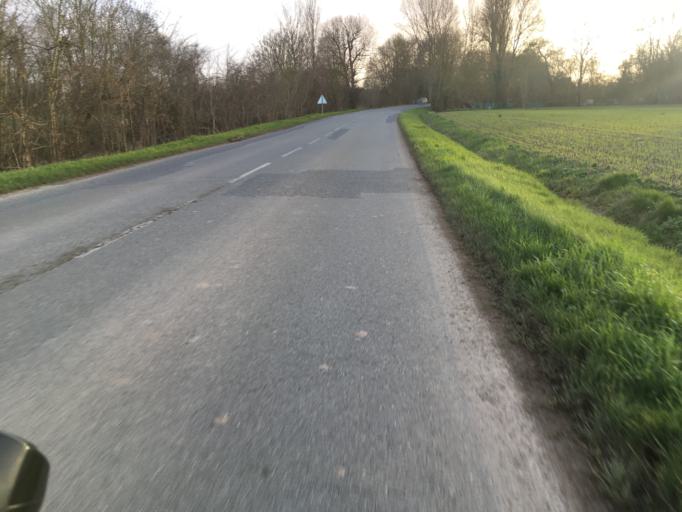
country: FR
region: Poitou-Charentes
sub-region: Departement de la Charente-Maritime
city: Courcon
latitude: 46.1699
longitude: -0.8496
